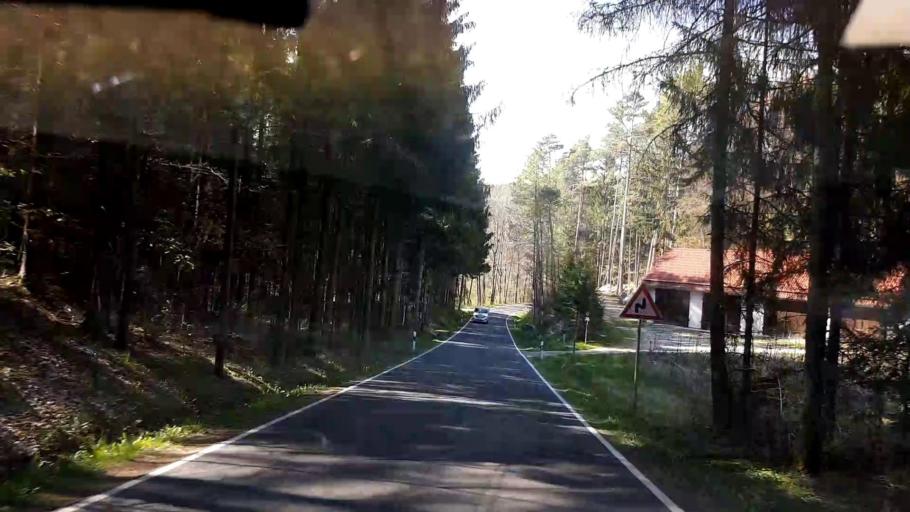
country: DE
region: Bavaria
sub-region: Upper Franconia
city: Pottenstein
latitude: 49.7947
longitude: 11.3781
